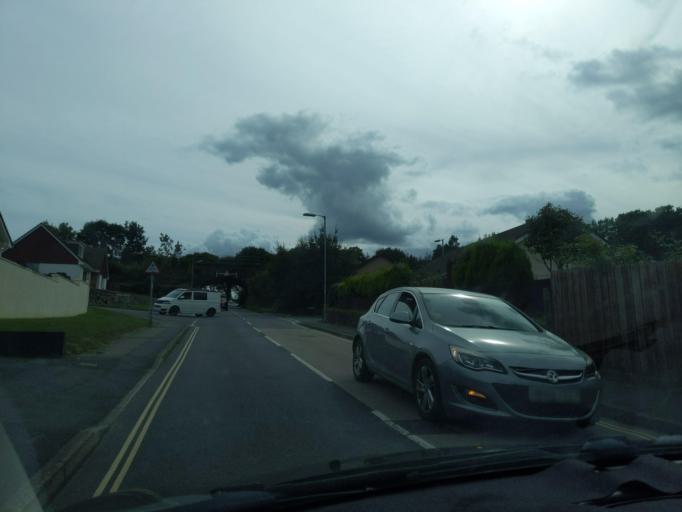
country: GB
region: England
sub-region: Cornwall
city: St Austell
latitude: 50.3390
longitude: -4.7591
